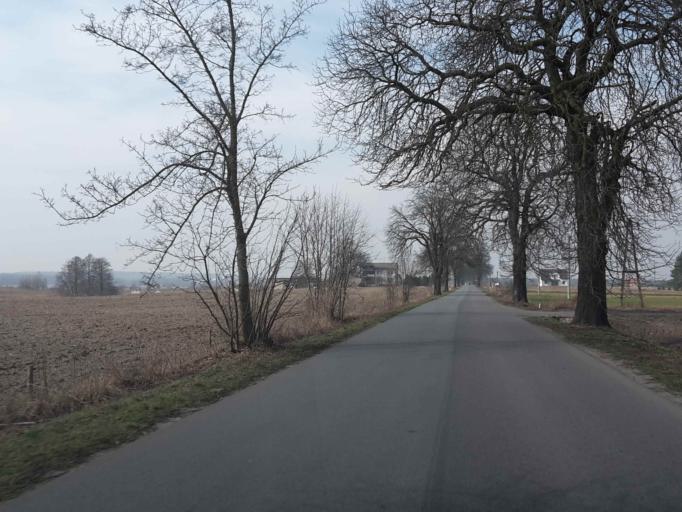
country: PL
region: Kujawsko-Pomorskie
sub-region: Powiat nakielski
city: Szubin
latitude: 53.0849
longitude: 17.7671
